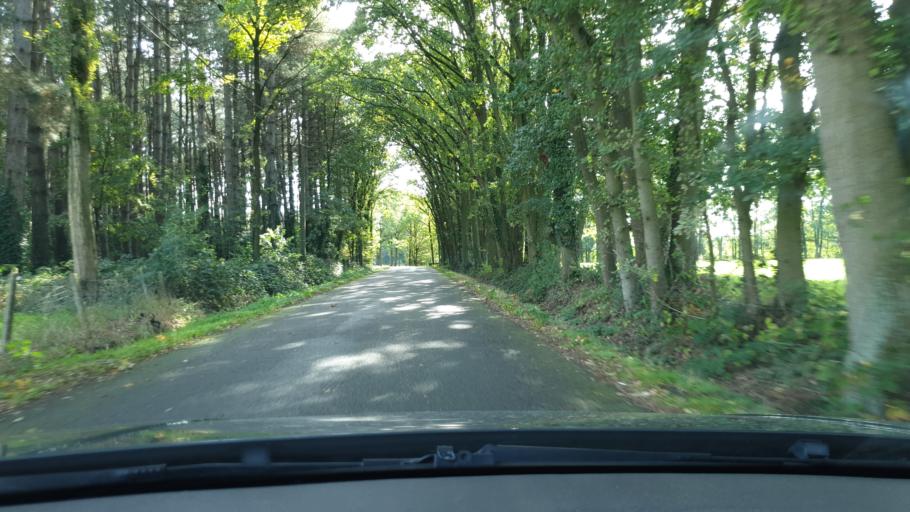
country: BE
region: Flanders
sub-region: Provincie Antwerpen
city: Geel
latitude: 51.1352
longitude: 4.9974
